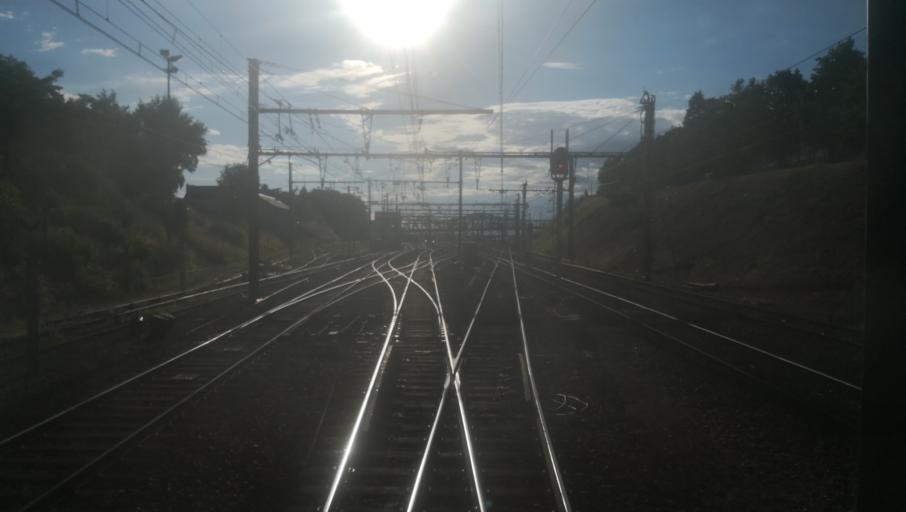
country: FR
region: Centre
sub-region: Departement du Cher
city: Vierzon
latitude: 47.2251
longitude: 2.0664
